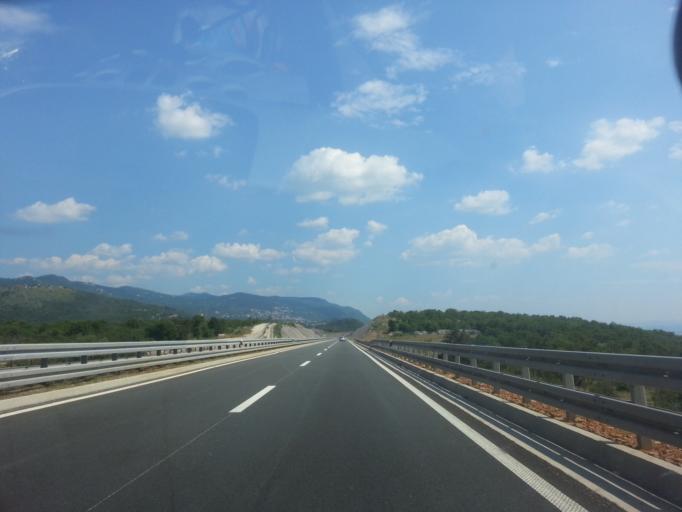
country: HR
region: Primorsko-Goranska
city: Krasica
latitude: 45.3080
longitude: 14.5494
